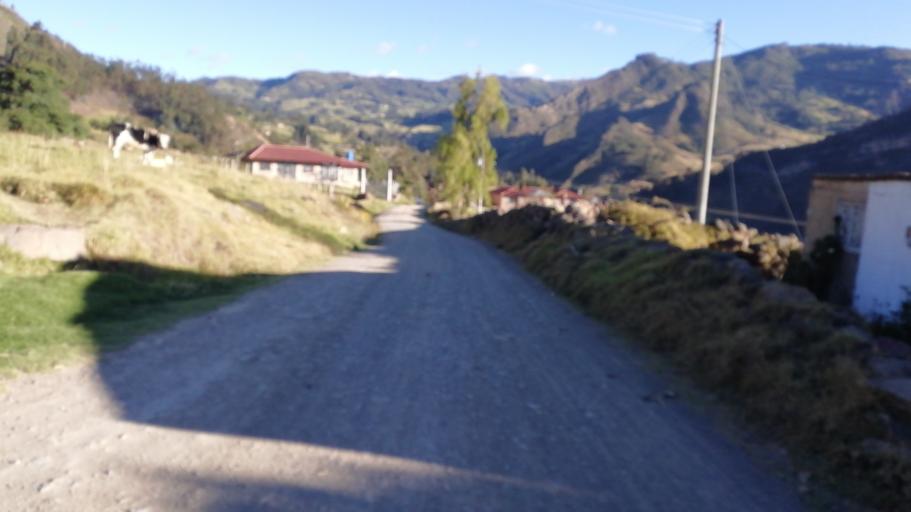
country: CO
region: Boyaca
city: Gameza
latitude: 5.7912
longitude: -72.8034
